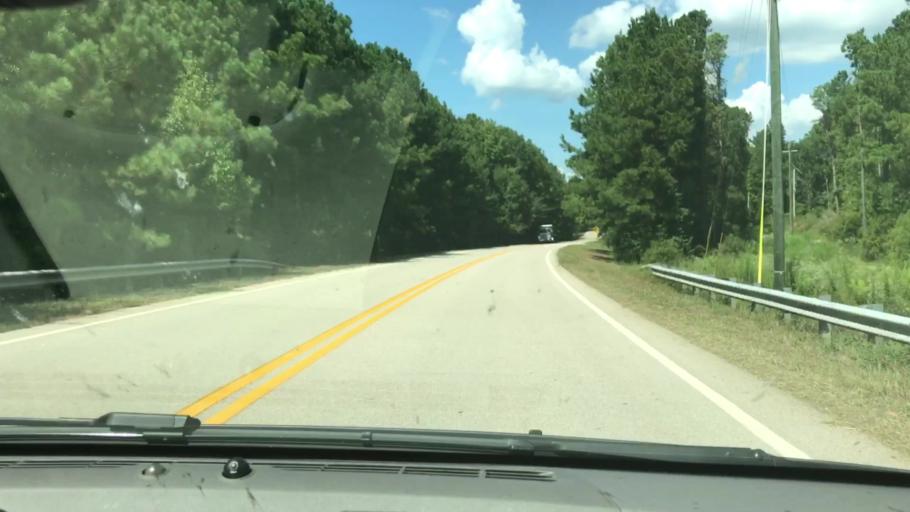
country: US
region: Georgia
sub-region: Troup County
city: La Grange
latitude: 33.1359
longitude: -85.0898
